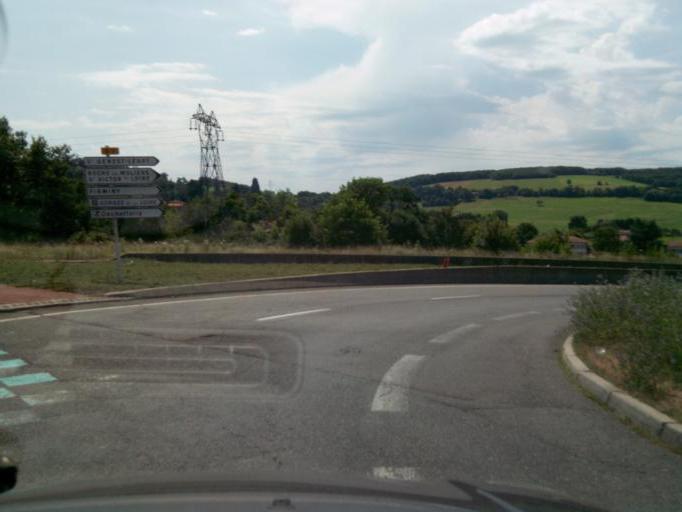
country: FR
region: Rhone-Alpes
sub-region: Departement de la Loire
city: Saint-Genest-Lerpt
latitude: 45.4335
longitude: 4.3450
